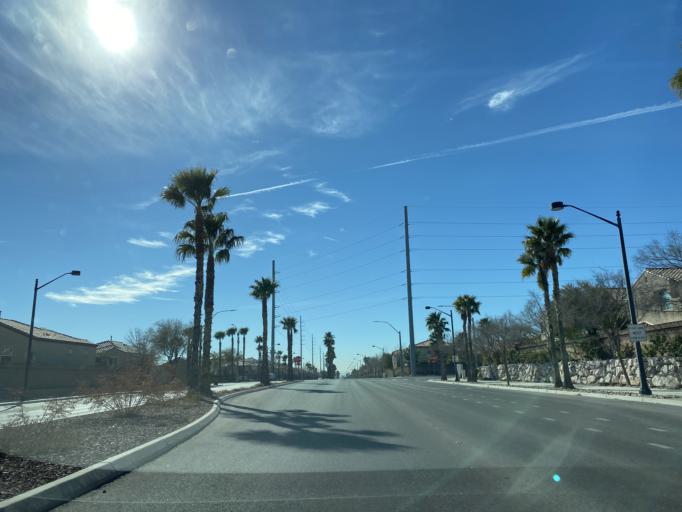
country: US
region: Nevada
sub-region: Clark County
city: Summerlin South
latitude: 36.3000
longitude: -115.2969
